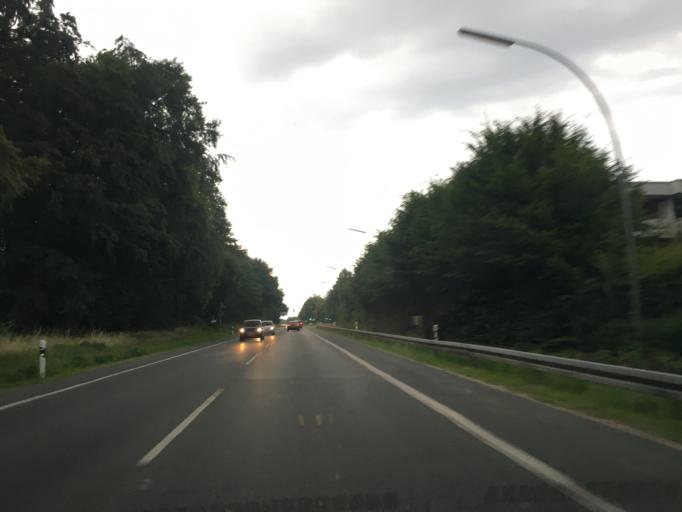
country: DE
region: North Rhine-Westphalia
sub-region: Regierungsbezirk Munster
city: Muenster
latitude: 51.9062
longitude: 7.6706
